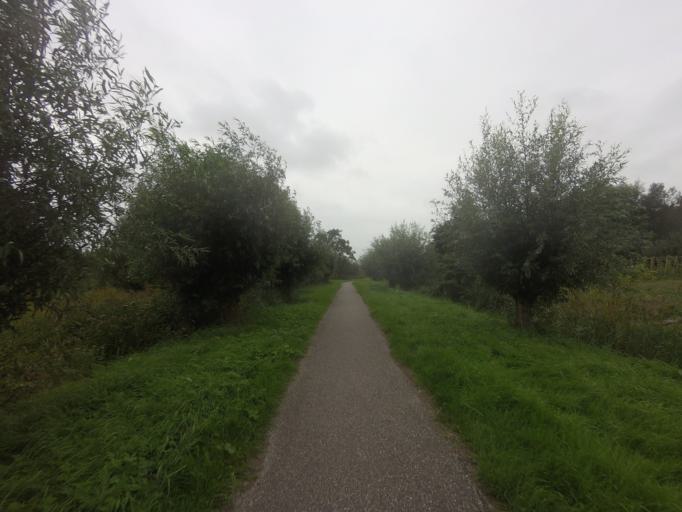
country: NL
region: Friesland
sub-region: Gemeente Leeuwarden
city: Bilgaard
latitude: 53.2250
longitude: 5.7924
